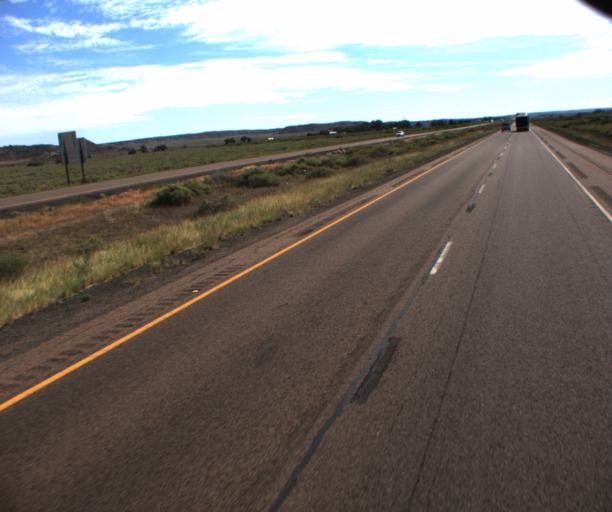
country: US
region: Arizona
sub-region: Apache County
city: Houck
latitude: 35.1944
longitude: -109.4163
